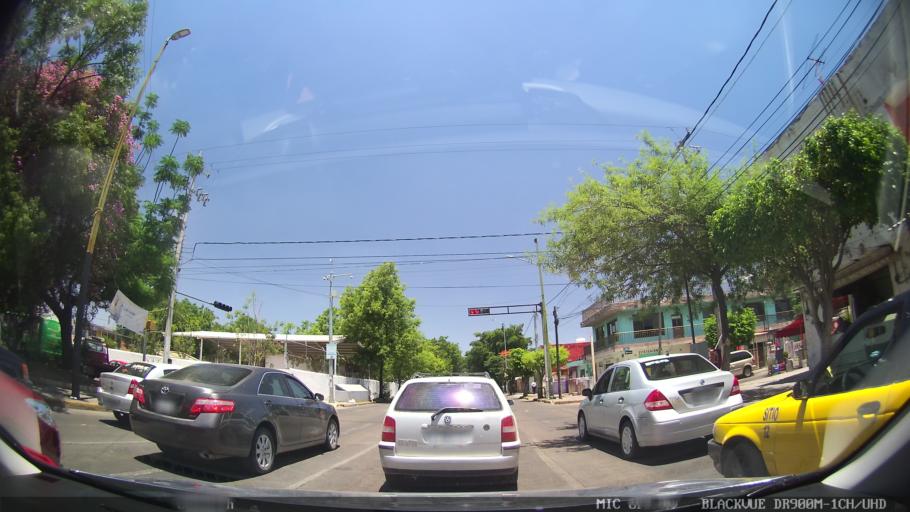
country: MX
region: Jalisco
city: Tlaquepaque
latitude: 20.6621
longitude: -103.2831
